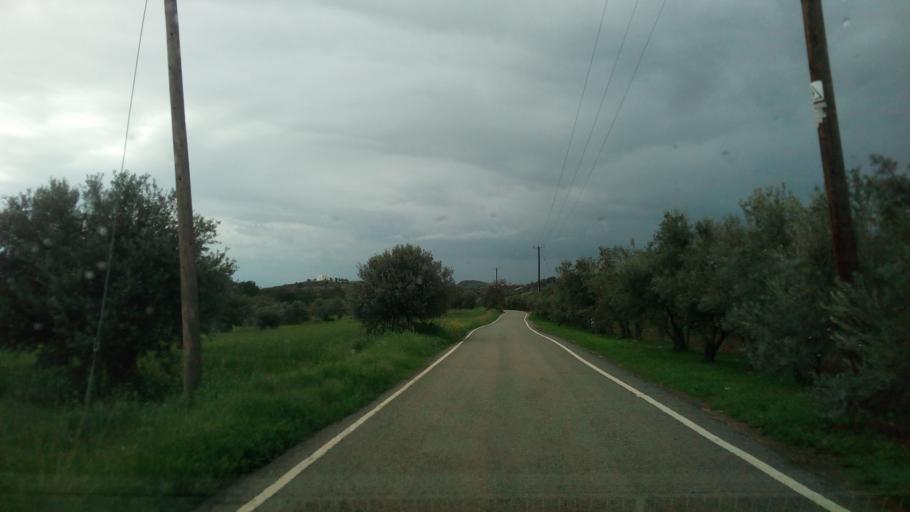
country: CY
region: Larnaka
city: Kofinou
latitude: 34.8693
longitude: 33.4500
